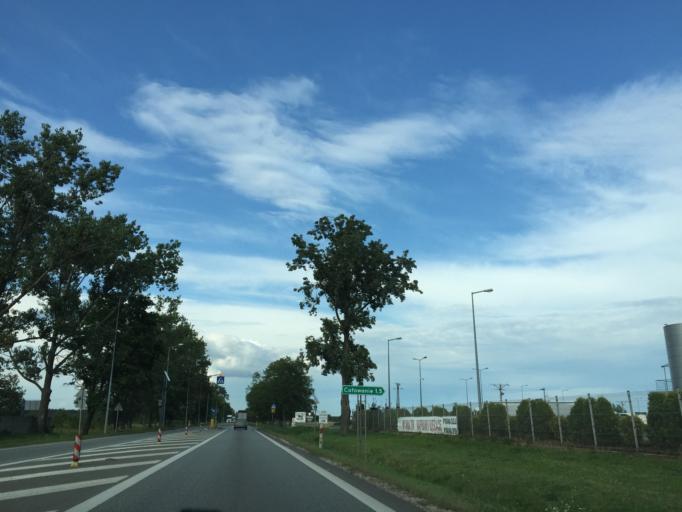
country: PL
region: Masovian Voivodeship
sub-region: Powiat otwocki
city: Karczew
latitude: 52.0172
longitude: 21.2904
